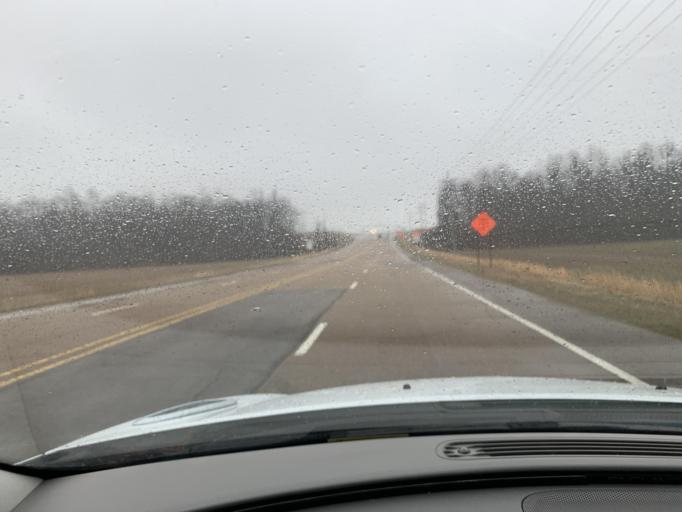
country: US
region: Mississippi
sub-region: De Soto County
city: Hernando
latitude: 34.8698
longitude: -89.9709
